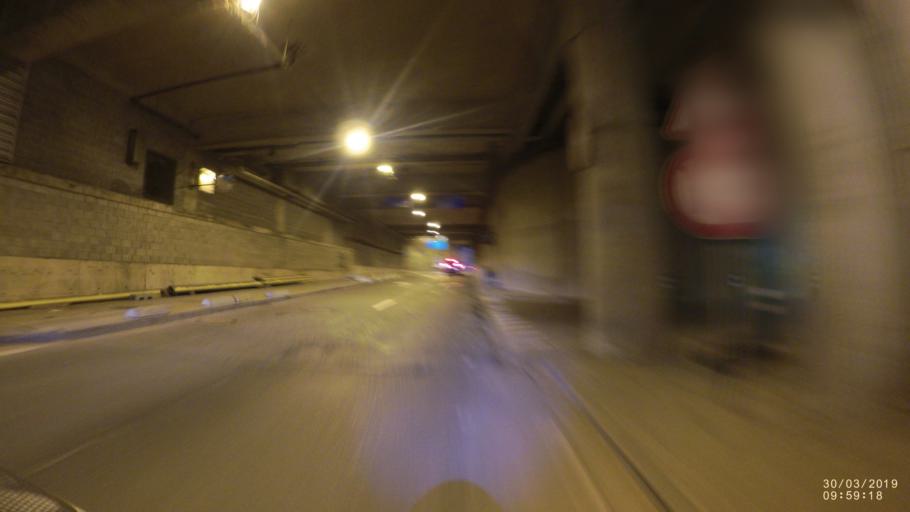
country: BE
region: Wallonia
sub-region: Province du Brabant Wallon
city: Louvain-la-Neuve
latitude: 50.6655
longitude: 4.6085
